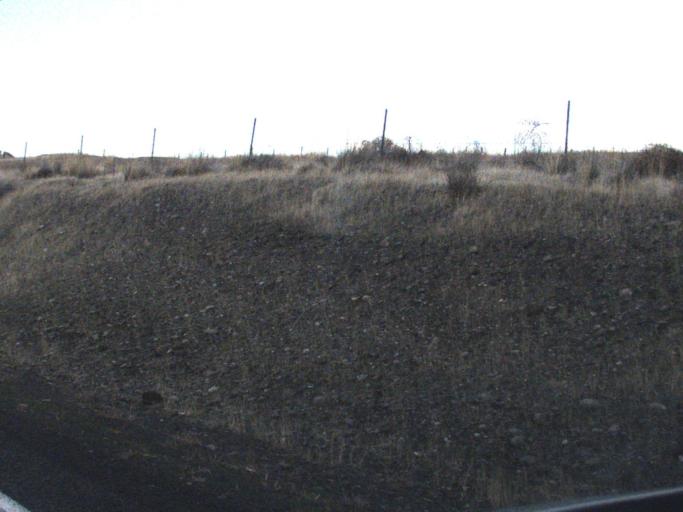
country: US
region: Washington
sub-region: Walla Walla County
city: Waitsburg
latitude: 46.5815
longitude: -118.2145
